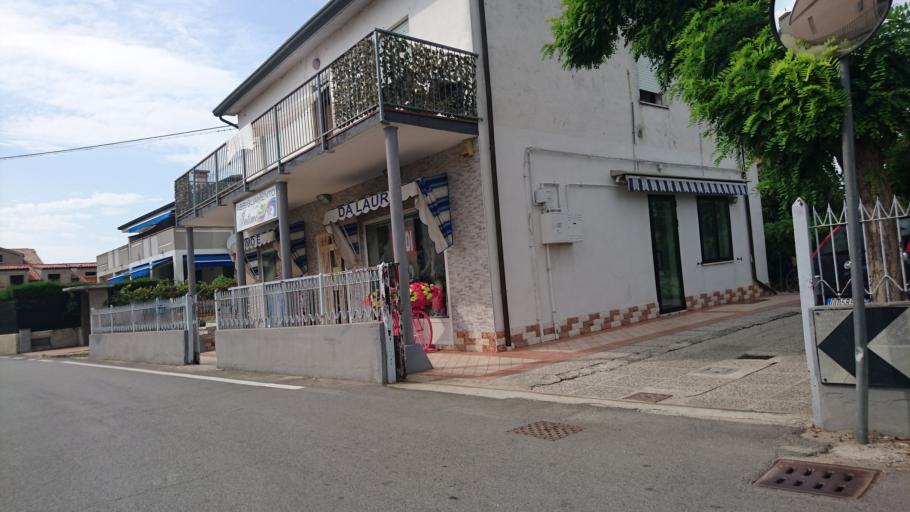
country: IT
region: Veneto
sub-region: Provincia di Venezia
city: Sant'Anna
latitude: 45.1456
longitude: 12.2684
